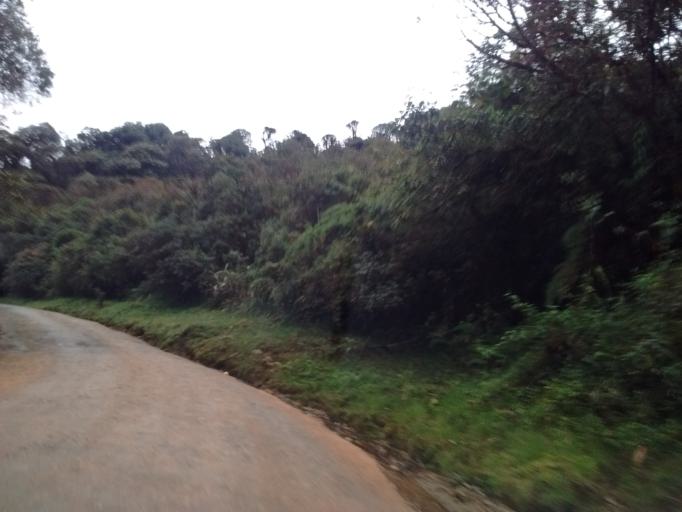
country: CO
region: Huila
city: Isnos
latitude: 2.1375
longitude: -76.3839
